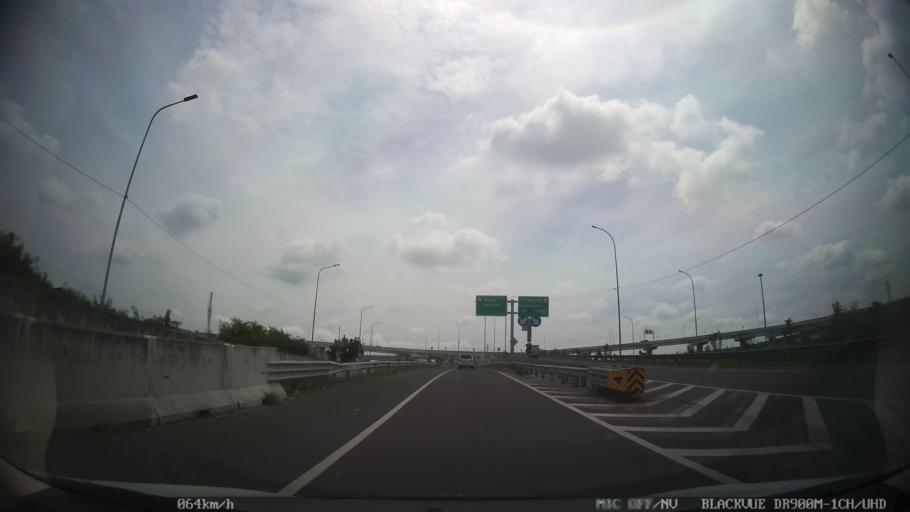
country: ID
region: North Sumatra
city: Medan
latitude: 3.6498
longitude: 98.6801
